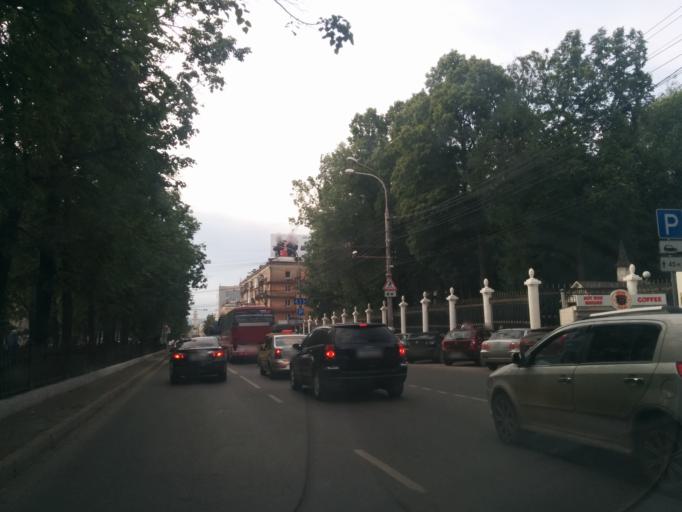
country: RU
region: Perm
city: Perm
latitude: 58.0042
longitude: 56.2457
